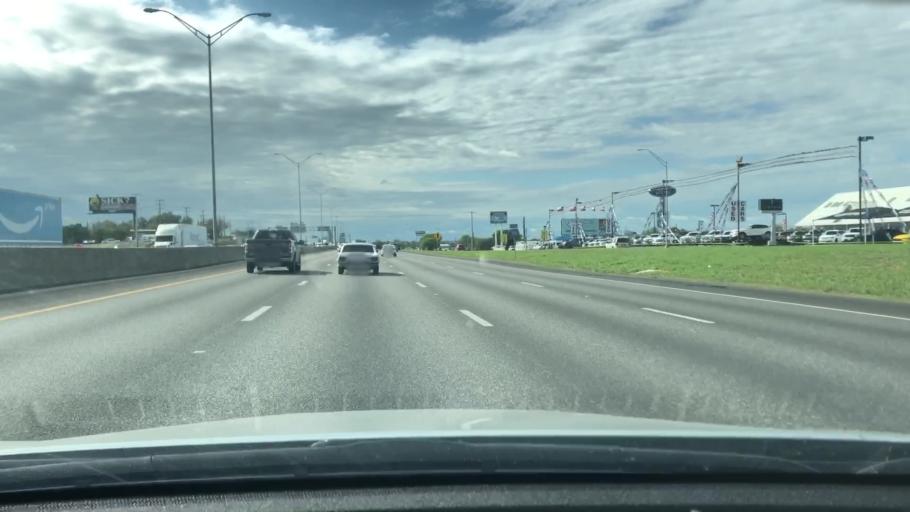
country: US
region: Texas
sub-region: Comal County
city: New Braunfels
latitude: 29.6857
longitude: -98.1341
